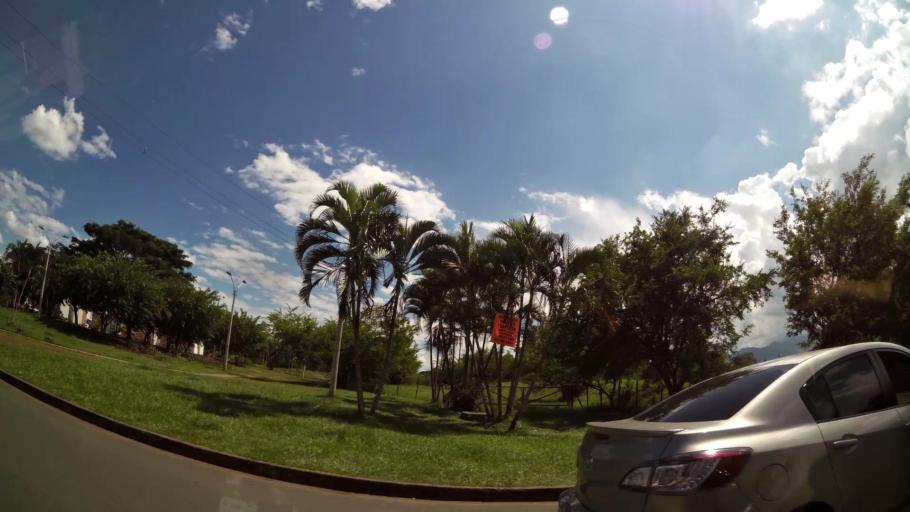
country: CO
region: Valle del Cauca
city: Cali
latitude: 3.3944
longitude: -76.5195
